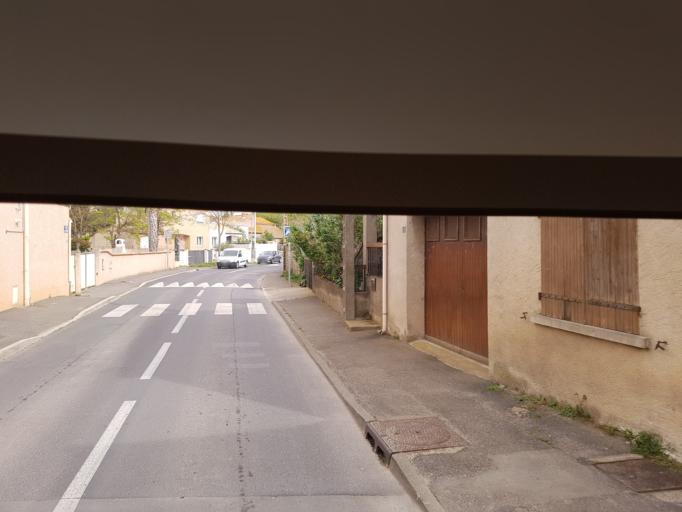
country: FR
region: Languedoc-Roussillon
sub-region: Departement de l'Herault
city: Vendres
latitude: 43.2692
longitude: 3.2205
